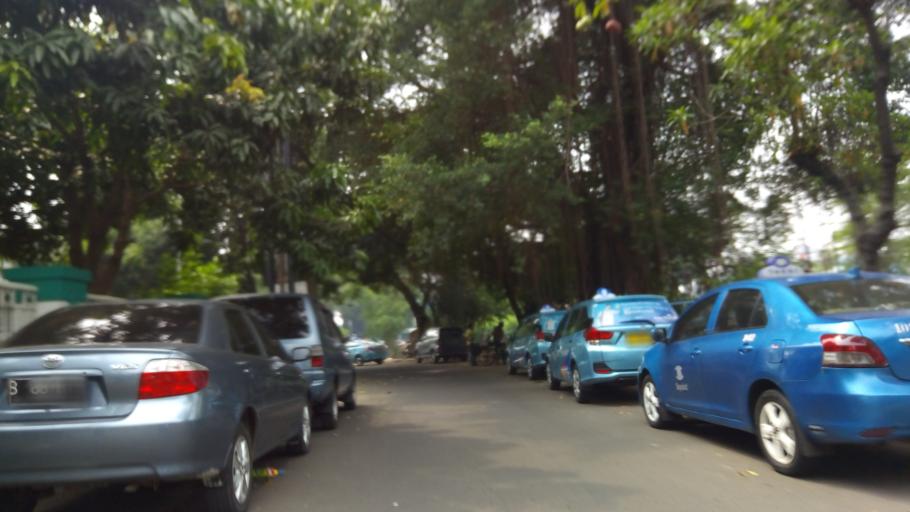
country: ID
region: Jakarta Raya
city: Jakarta
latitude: -6.1638
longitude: 106.8375
